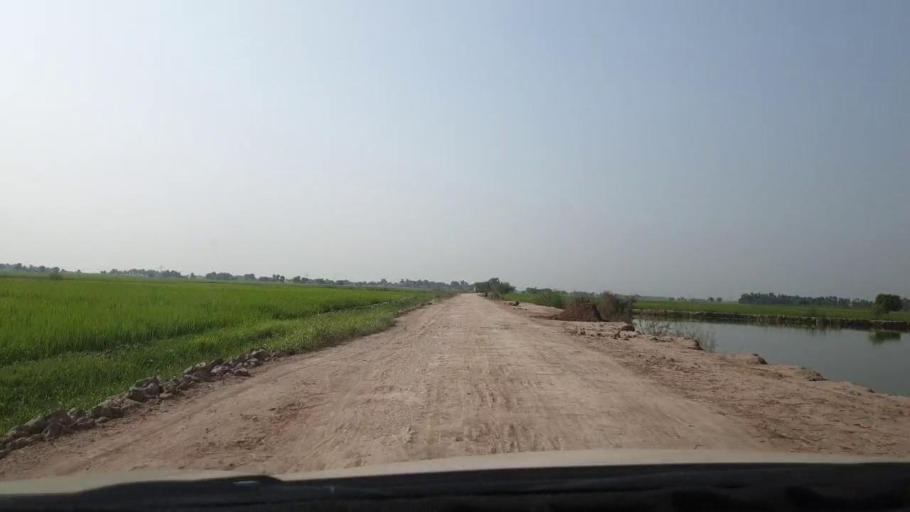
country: PK
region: Sindh
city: Goth Garelo
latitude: 27.4728
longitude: 68.0877
